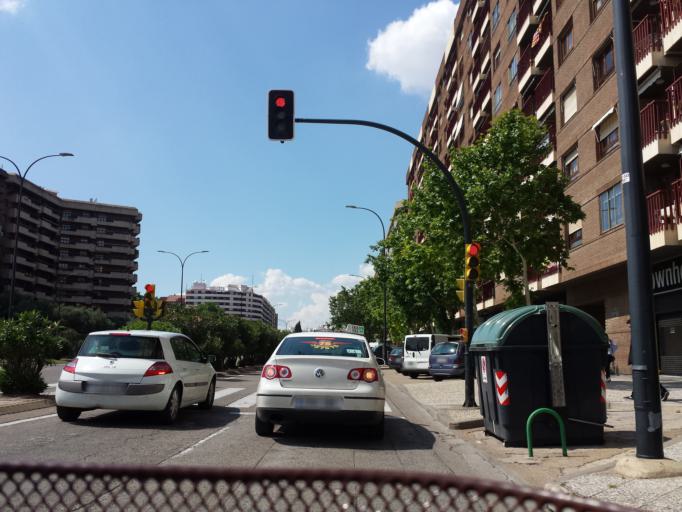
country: ES
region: Aragon
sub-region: Provincia de Zaragoza
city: Zaragoza
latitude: 41.6426
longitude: -0.8754
